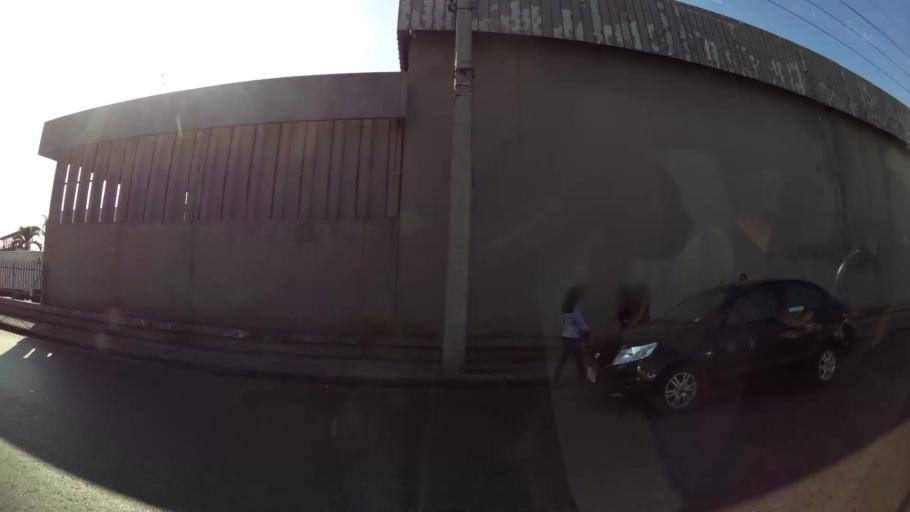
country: EC
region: Guayas
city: Guayaquil
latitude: -2.1701
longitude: -79.9008
